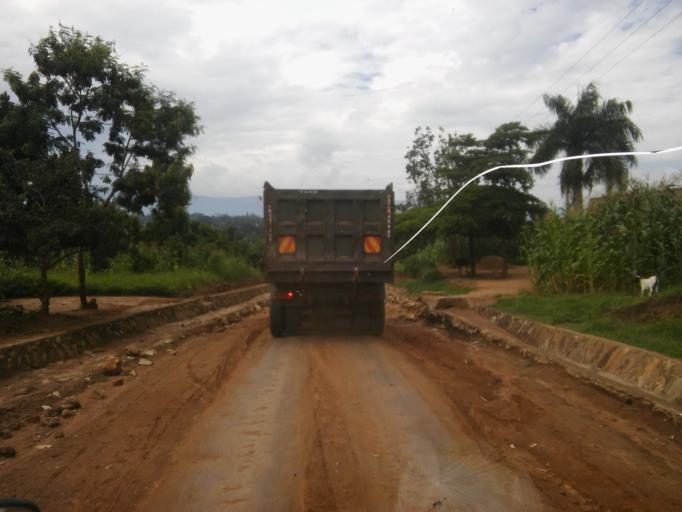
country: KE
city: Malikisi
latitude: 0.8136
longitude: 34.3423
